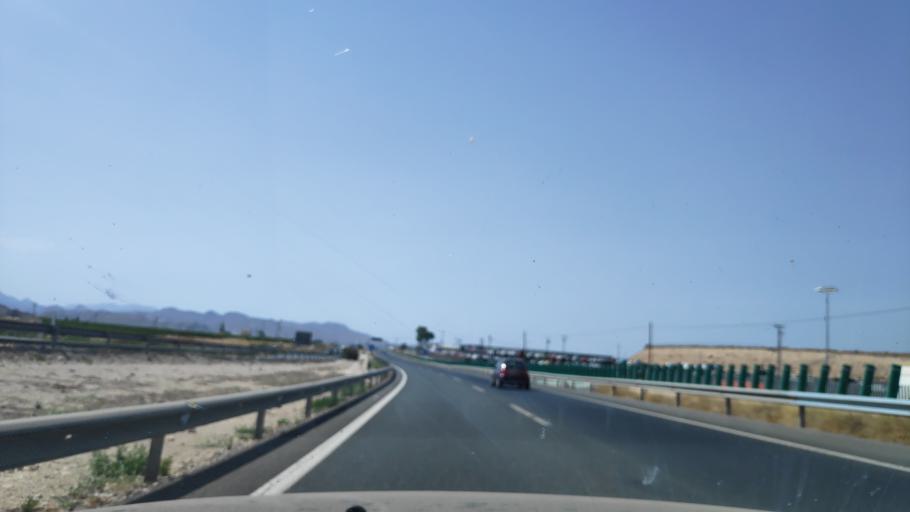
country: ES
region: Murcia
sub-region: Murcia
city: Lorqui
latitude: 38.1161
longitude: -1.2420
